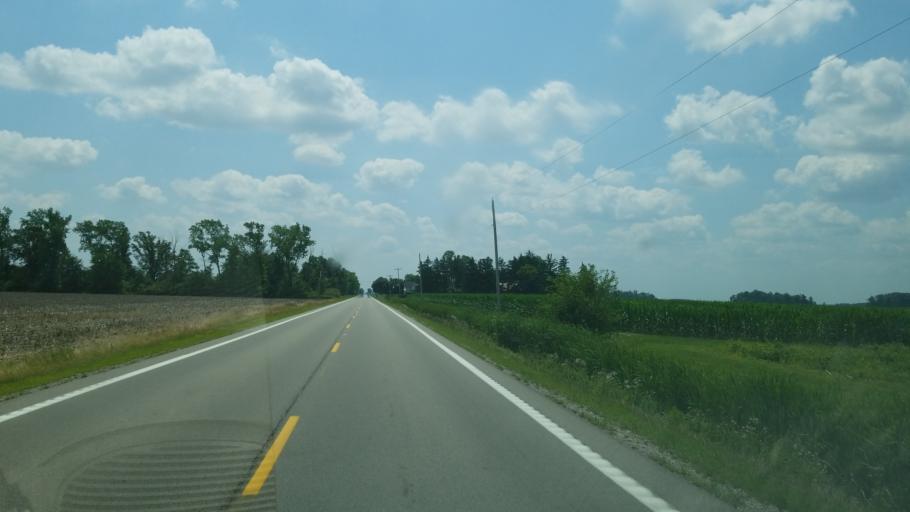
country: US
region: Ohio
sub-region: Henry County
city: Deshler
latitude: 41.2731
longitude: -83.9406
